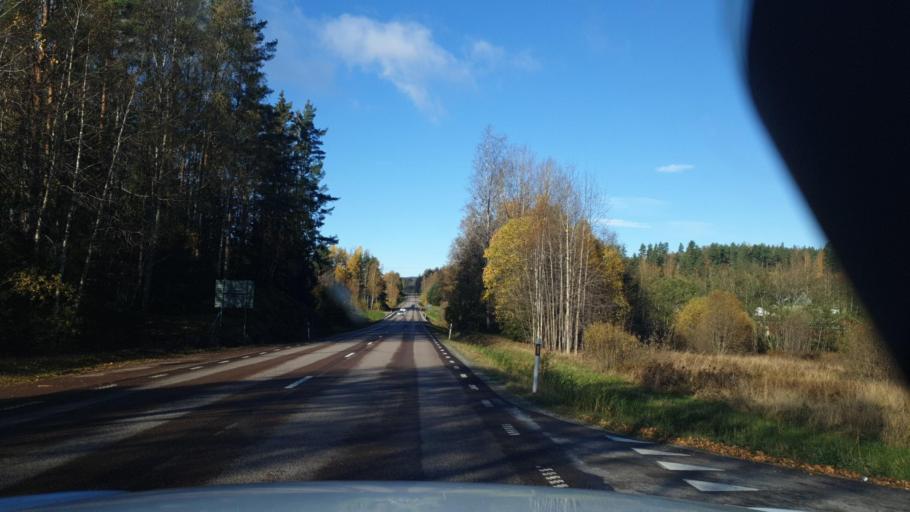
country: SE
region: Vaermland
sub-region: Sunne Kommun
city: Sunne
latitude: 59.6610
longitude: 12.9280
